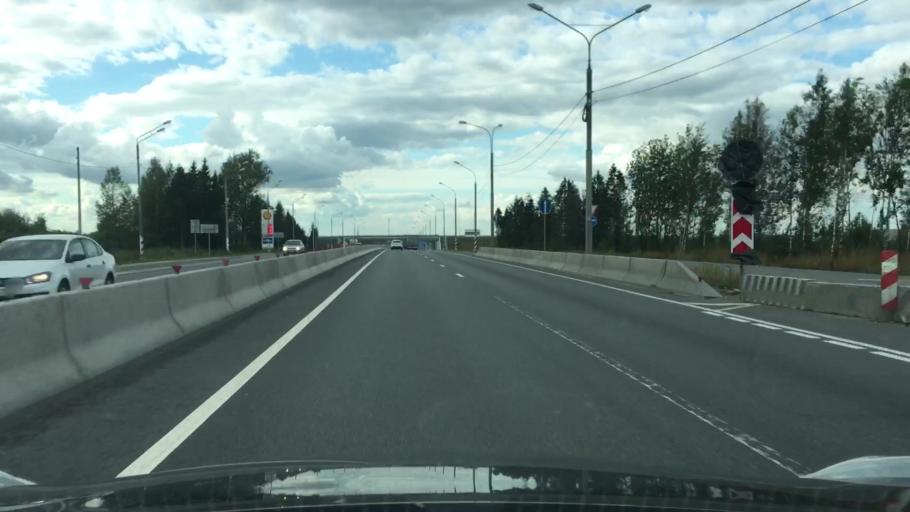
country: RU
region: Tverskaya
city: Tver
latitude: 56.7858
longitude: 35.9289
